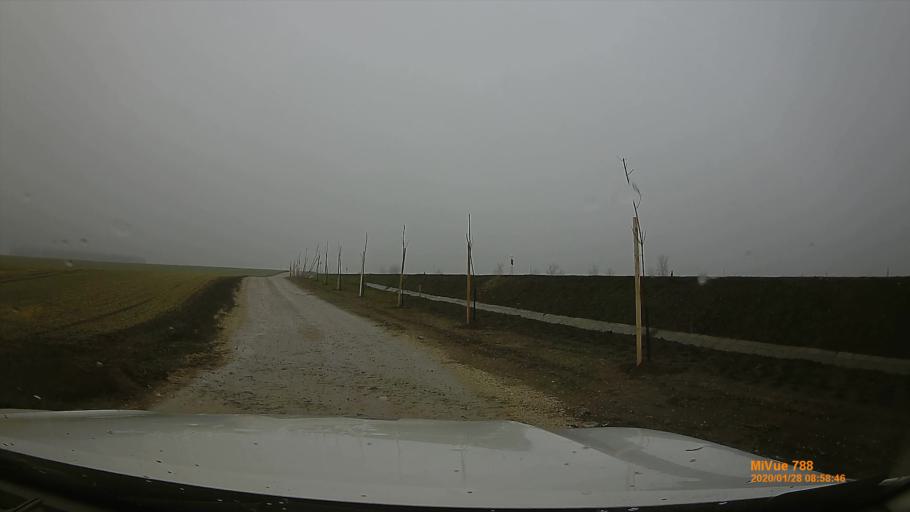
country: HU
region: Pest
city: Pilis
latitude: 47.3082
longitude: 19.5426
